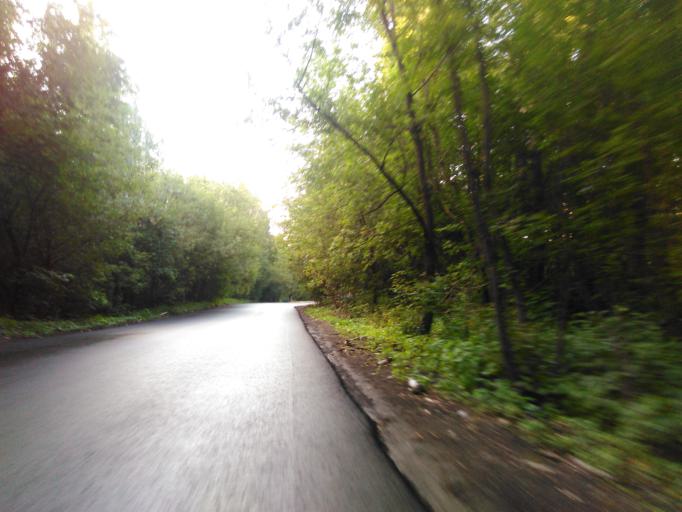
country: RU
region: Moskovskaya
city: Bogorodskoye
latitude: 55.8230
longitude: 37.6948
